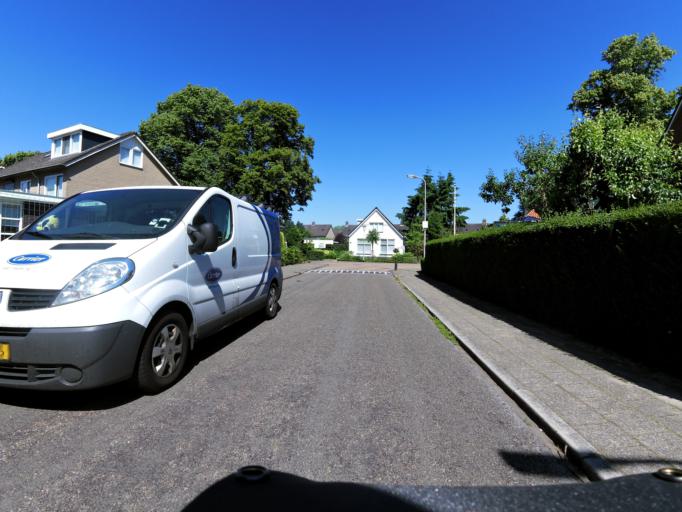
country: NL
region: Overijssel
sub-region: Gemeente Twenterand
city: Den Ham
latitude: 52.5228
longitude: 6.4372
